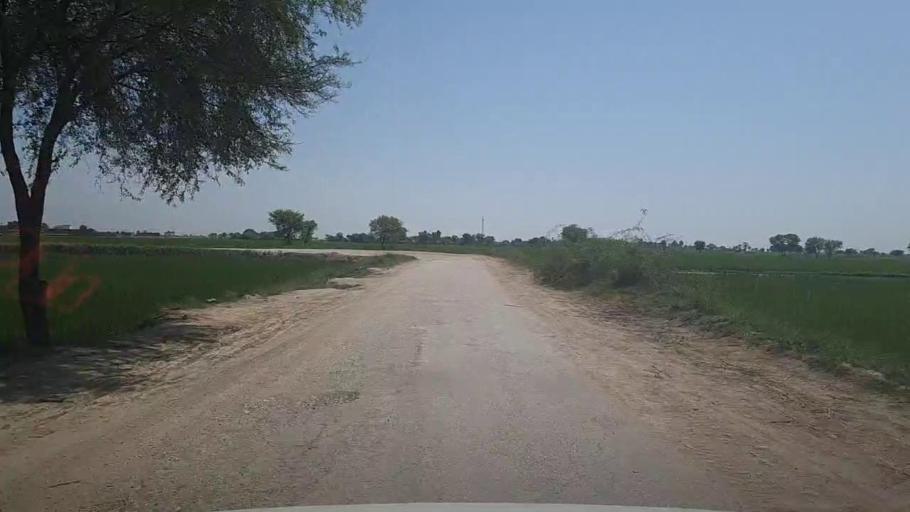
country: PK
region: Sindh
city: Kashmor
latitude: 28.2926
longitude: 69.4339
